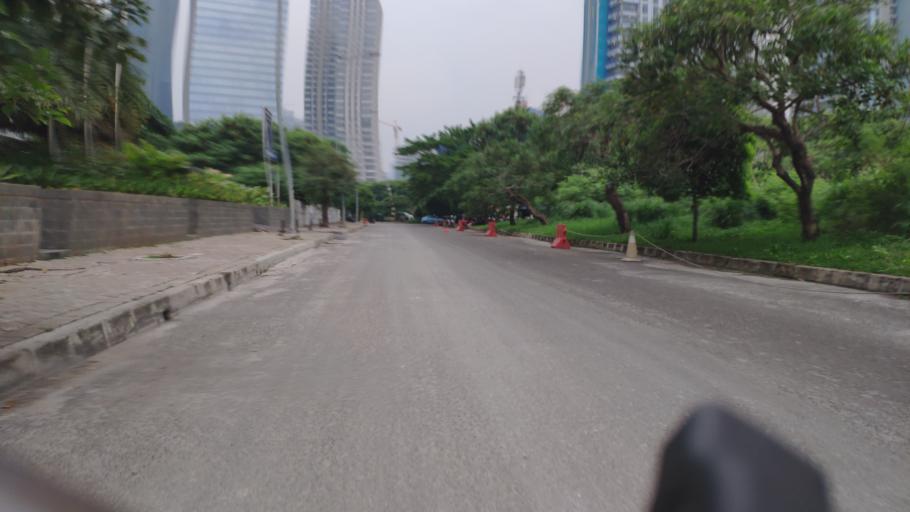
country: ID
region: Jakarta Raya
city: Jakarta
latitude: -6.2136
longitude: 106.8369
